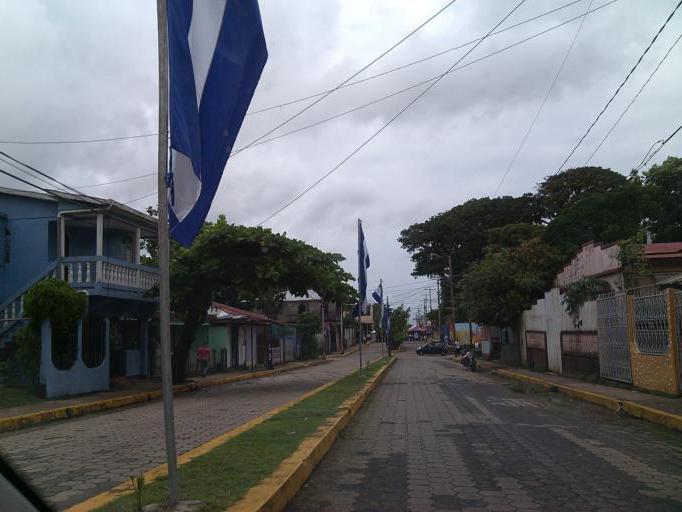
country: NI
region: Atlantico Sur
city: Bluefields
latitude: 12.0145
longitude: -83.7646
